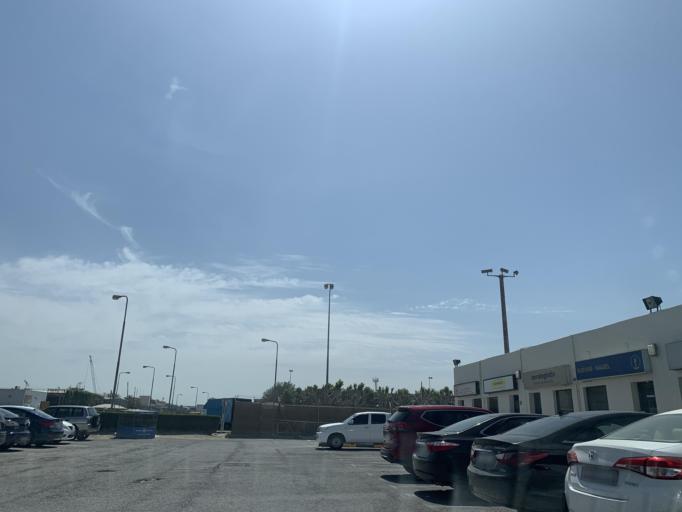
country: BH
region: Muharraq
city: Al Muharraq
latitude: 26.2721
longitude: 50.6198
